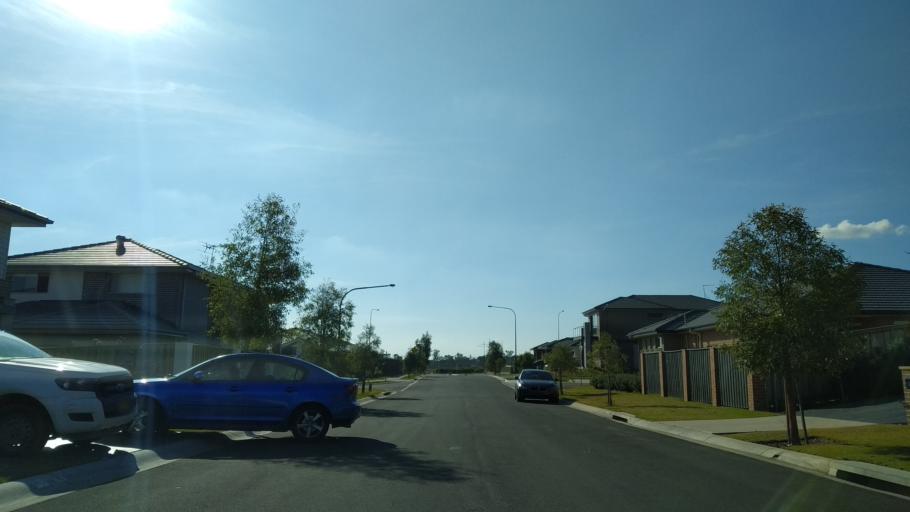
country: AU
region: New South Wales
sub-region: Blacktown
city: Hassall Grove
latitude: -33.7239
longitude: 150.8520
